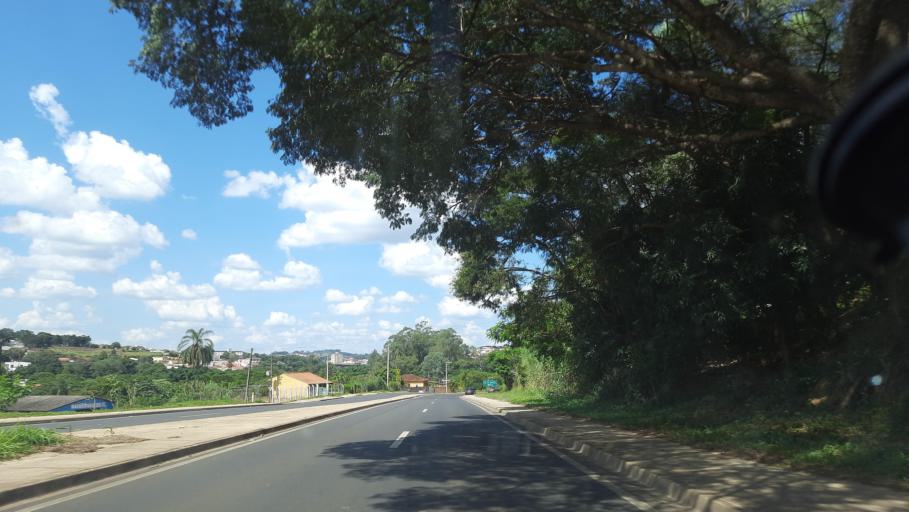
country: BR
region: Sao Paulo
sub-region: Sao Jose Do Rio Pardo
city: Sao Jose do Rio Pardo
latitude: -21.6017
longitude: -46.9076
